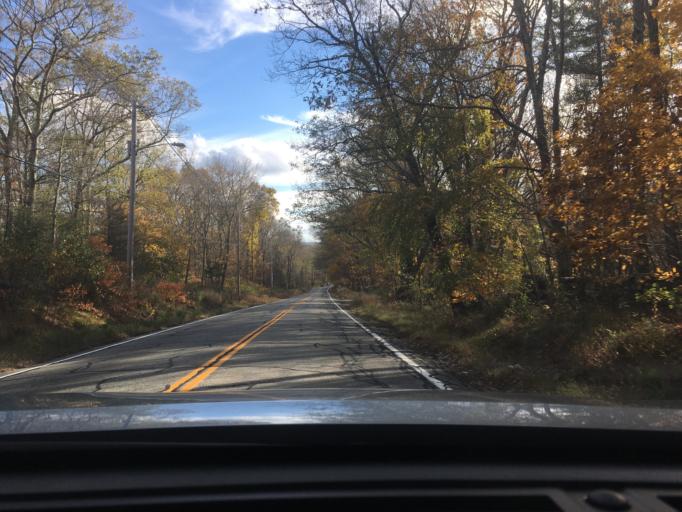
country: US
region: Rhode Island
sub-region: Providence County
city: North Scituate
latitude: 41.8001
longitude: -71.6581
